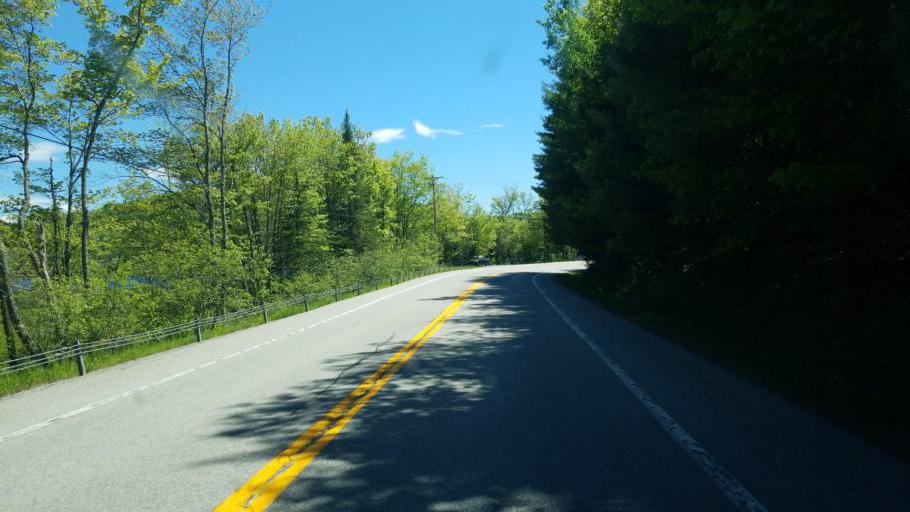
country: US
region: New York
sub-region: Fulton County
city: Gloversville
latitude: 43.2310
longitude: -74.5154
